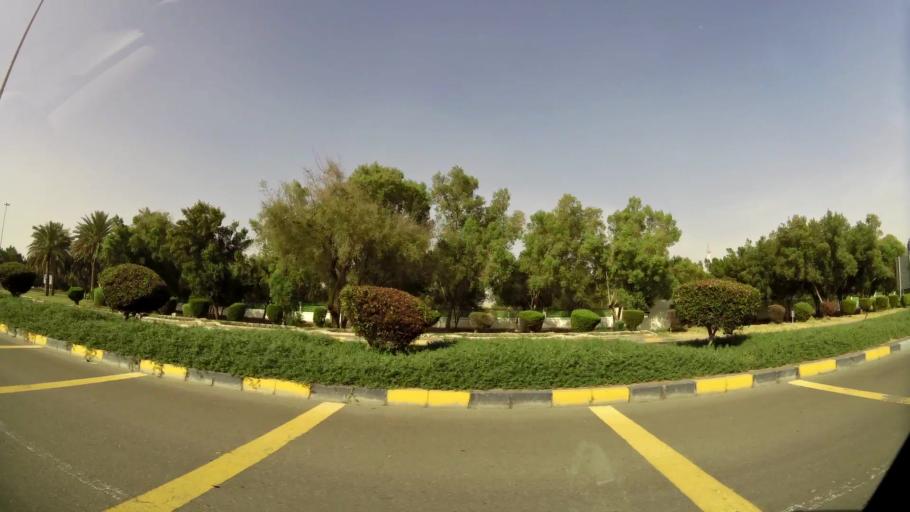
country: AE
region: Abu Dhabi
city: Al Ain
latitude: 24.1030
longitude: 55.7198
